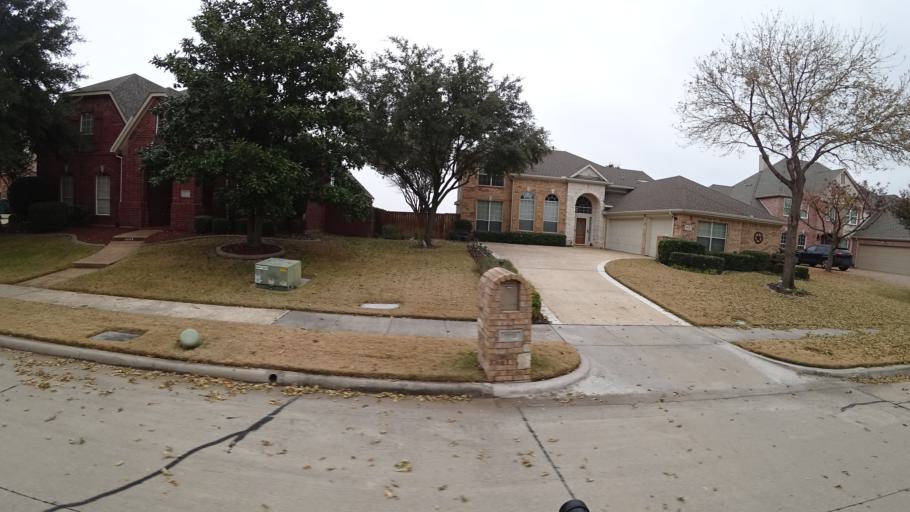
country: US
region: Texas
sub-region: Denton County
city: Lewisville
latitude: 33.0298
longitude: -96.9360
